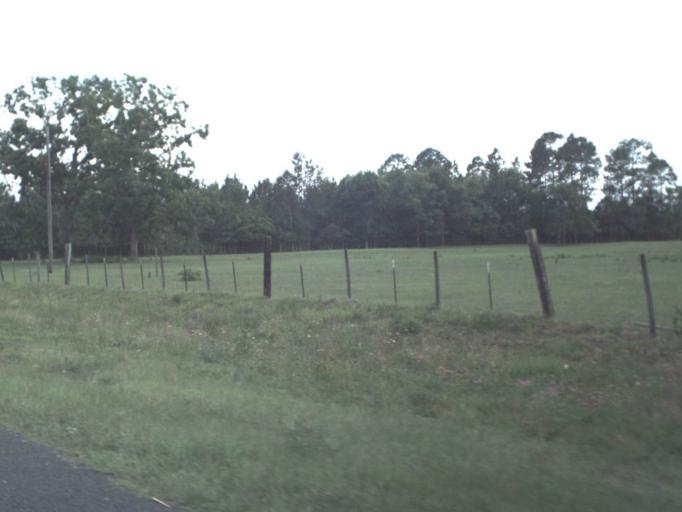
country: US
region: Florida
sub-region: Clay County
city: Green Cove Springs
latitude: 29.8619
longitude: -81.6634
